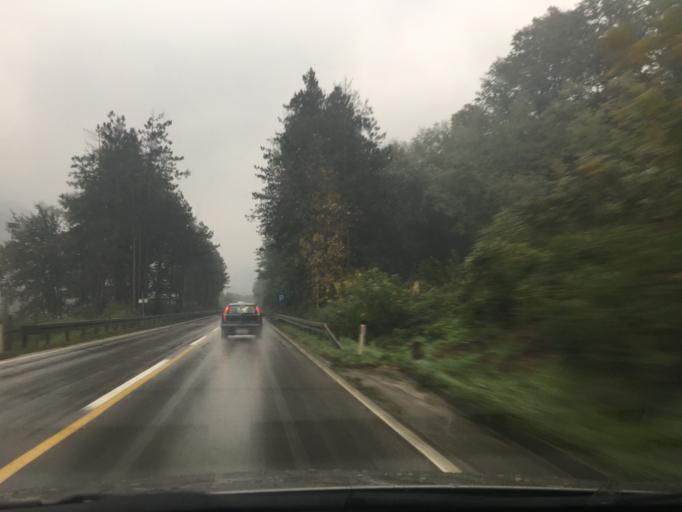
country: RS
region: Central Serbia
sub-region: Pcinjski Okrug
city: Vladicin Han
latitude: 42.8196
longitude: 22.1238
